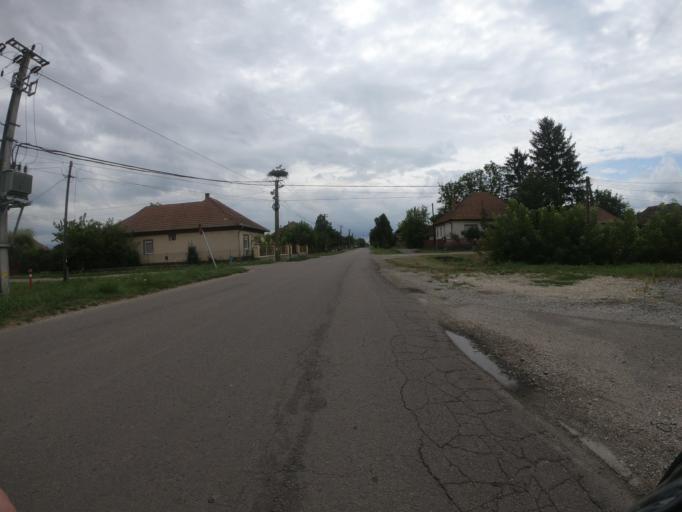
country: HU
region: Borsod-Abauj-Zemplen
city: Szentistvan
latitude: 47.7699
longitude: 20.6666
